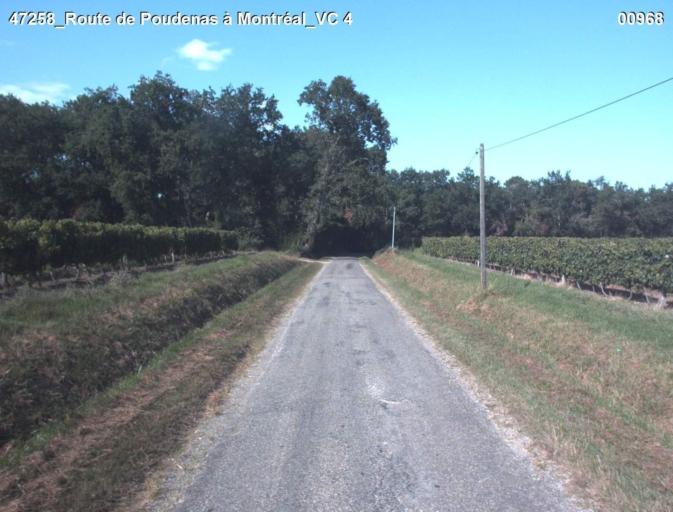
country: FR
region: Midi-Pyrenees
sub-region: Departement du Gers
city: Montreal
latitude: 44.0116
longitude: 0.1870
